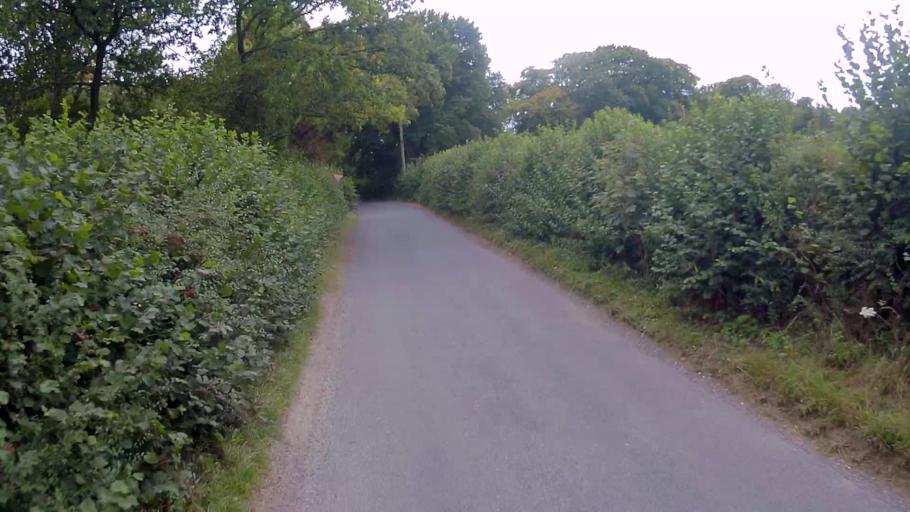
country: GB
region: England
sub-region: Hampshire
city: Overton
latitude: 51.1919
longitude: -1.2483
